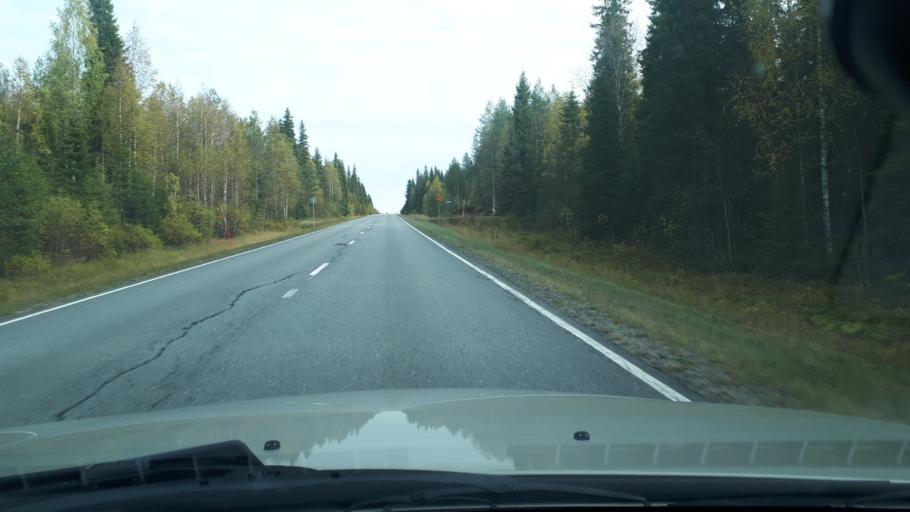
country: FI
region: Lapland
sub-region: Rovaniemi
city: Ranua
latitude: 65.9733
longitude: 26.1088
